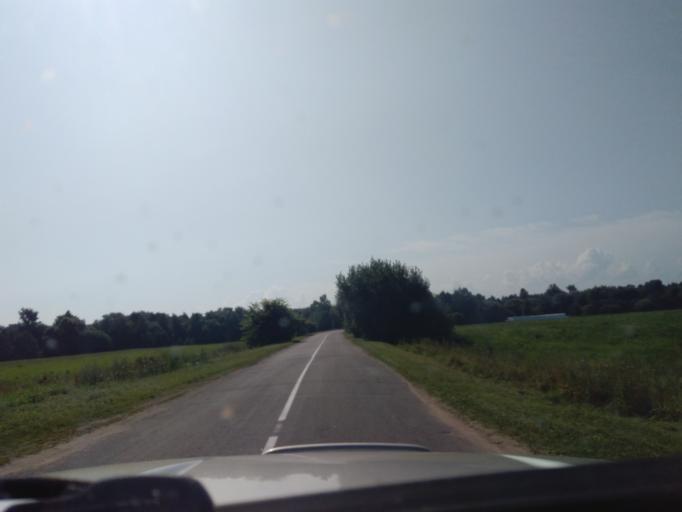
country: BY
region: Minsk
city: Valozhyn
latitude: 54.0164
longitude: 26.6043
